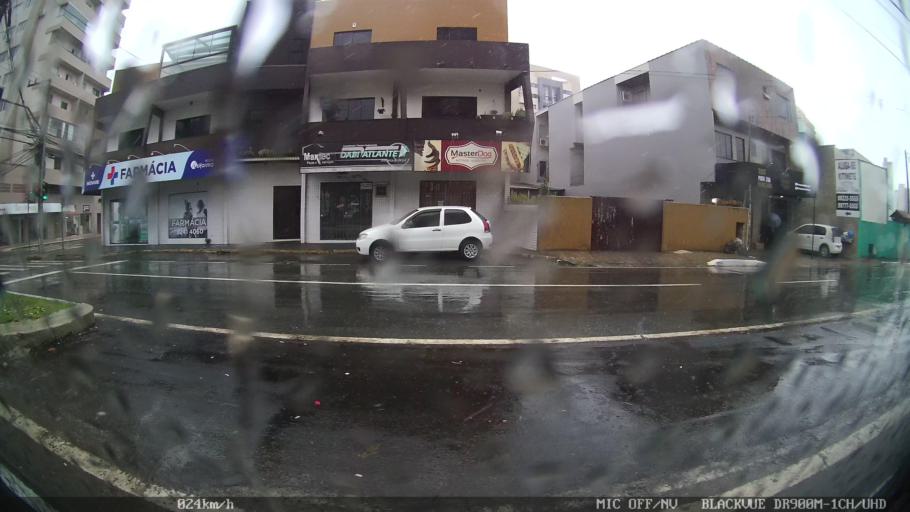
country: BR
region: Santa Catarina
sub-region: Itajai
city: Itajai
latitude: -26.9135
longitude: -48.6608
